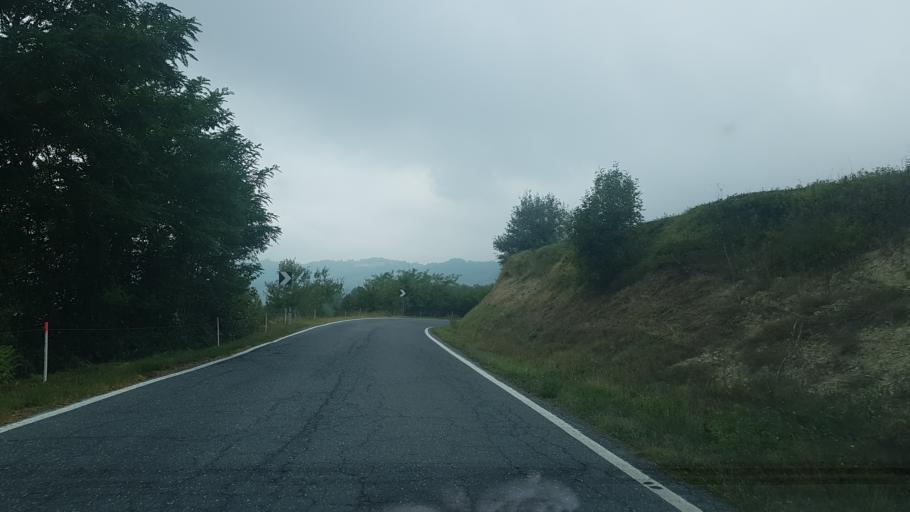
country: IT
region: Piedmont
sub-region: Provincia di Cuneo
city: Paroldo
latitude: 44.4307
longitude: 8.0860
